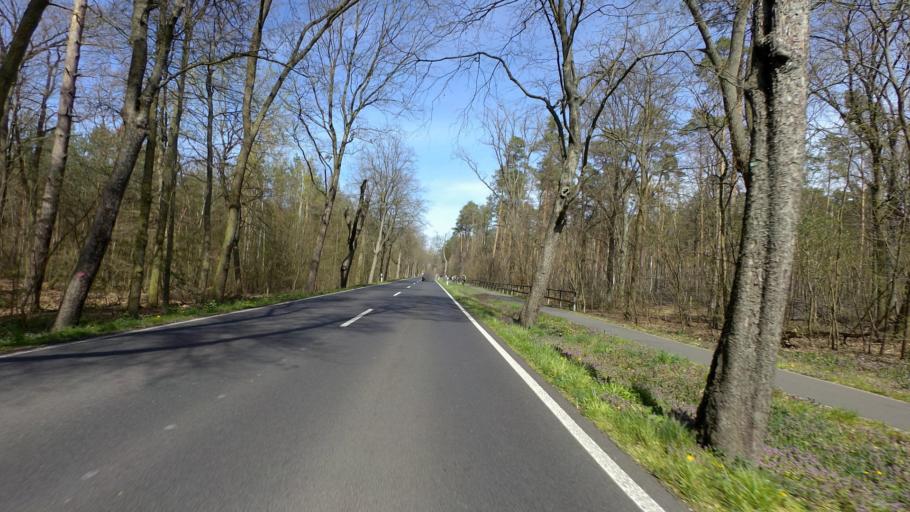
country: DE
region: Brandenburg
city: Grossbeeren
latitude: 52.3638
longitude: 13.3607
